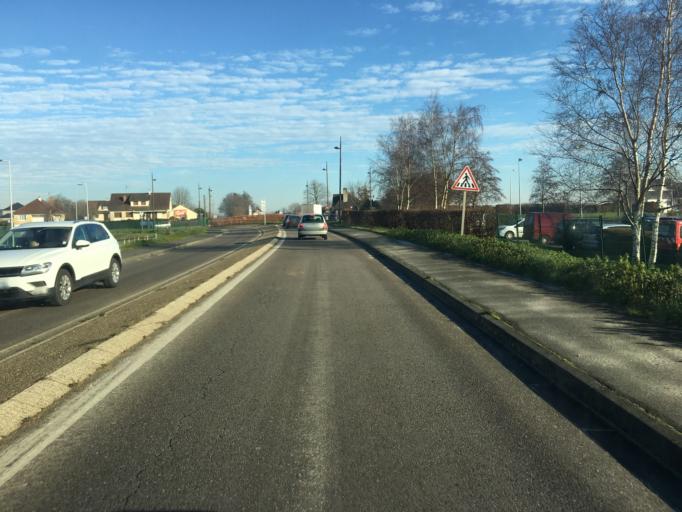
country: FR
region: Haute-Normandie
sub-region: Departement de la Seine-Maritime
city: Yvetot
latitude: 49.6071
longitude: 0.7671
